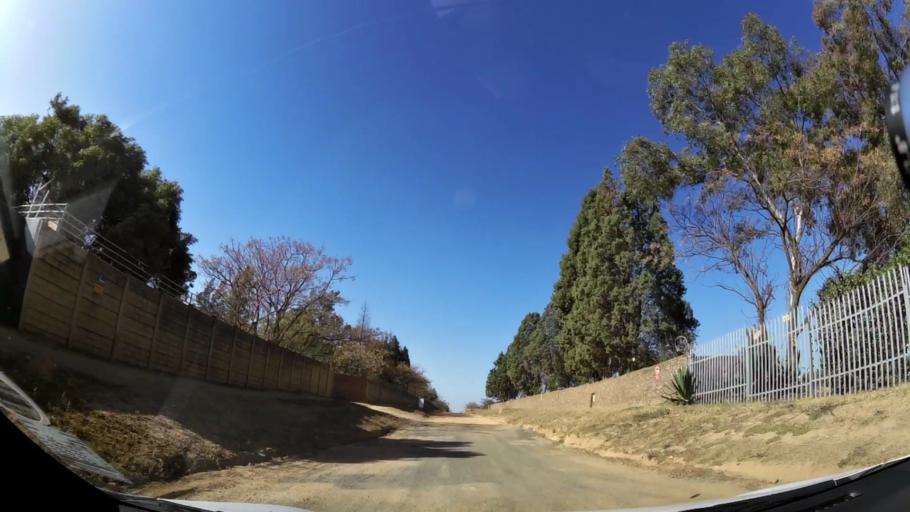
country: ZA
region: Gauteng
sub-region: City of Johannesburg Metropolitan Municipality
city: Diepsloot
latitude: -26.0110
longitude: 27.9546
